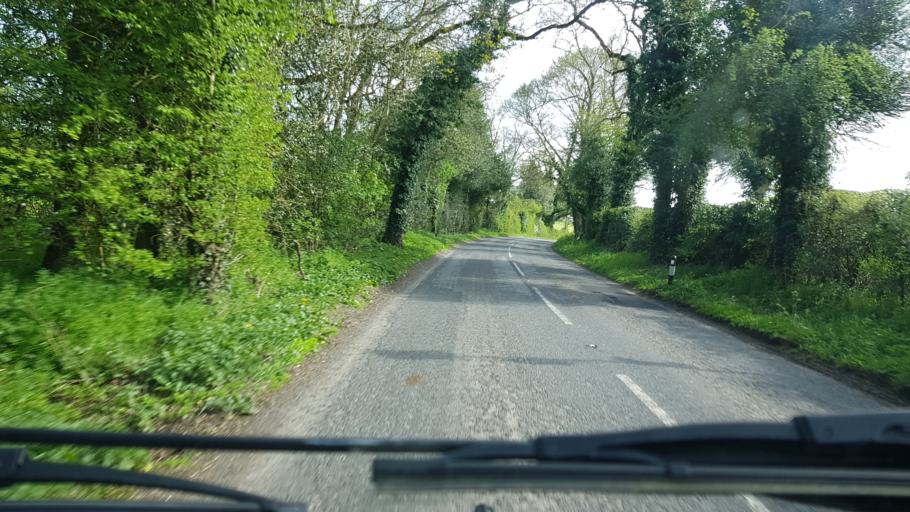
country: GB
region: England
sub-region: Hampshire
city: Kingsclere
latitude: 51.2872
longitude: -1.2627
